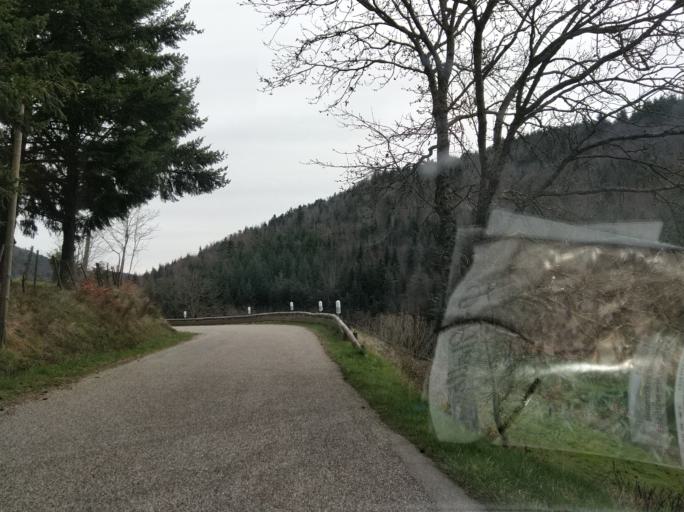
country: FR
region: Rhone-Alpes
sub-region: Departement de l'Ardeche
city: Satillieu
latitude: 45.1576
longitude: 4.5842
